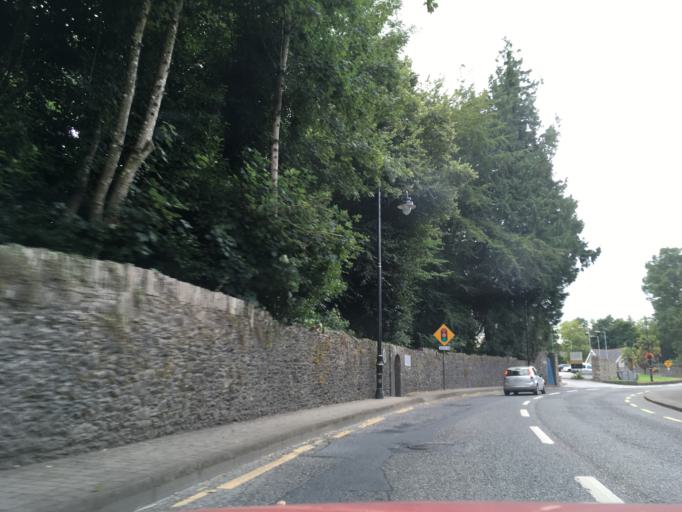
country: IE
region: Munster
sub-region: County Cork
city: Youghal
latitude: 52.1389
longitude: -7.9315
